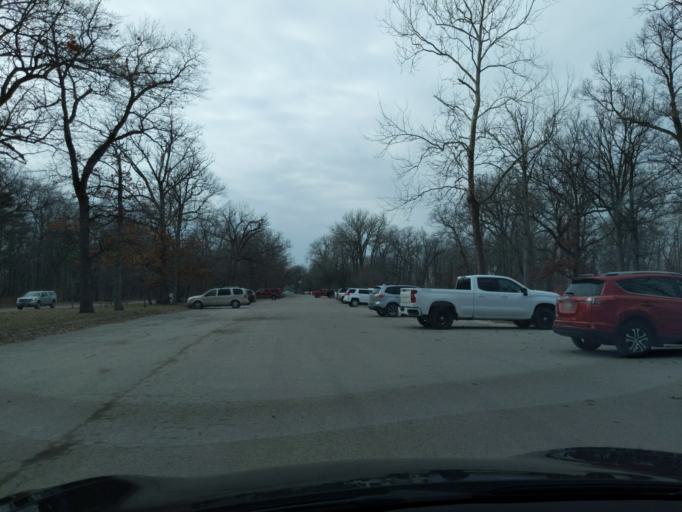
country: US
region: Michigan
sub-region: Bay County
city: Bay City
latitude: 43.6680
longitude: -83.9068
